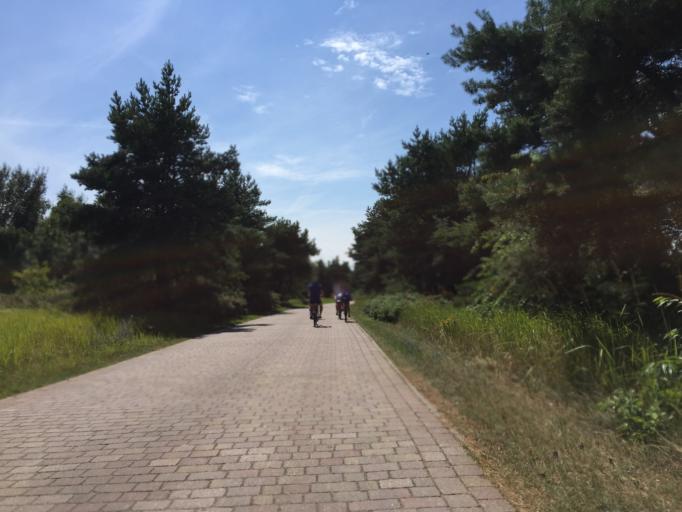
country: DE
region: Mecklenburg-Vorpommern
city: Hiddensee
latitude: 54.5346
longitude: 13.0896
